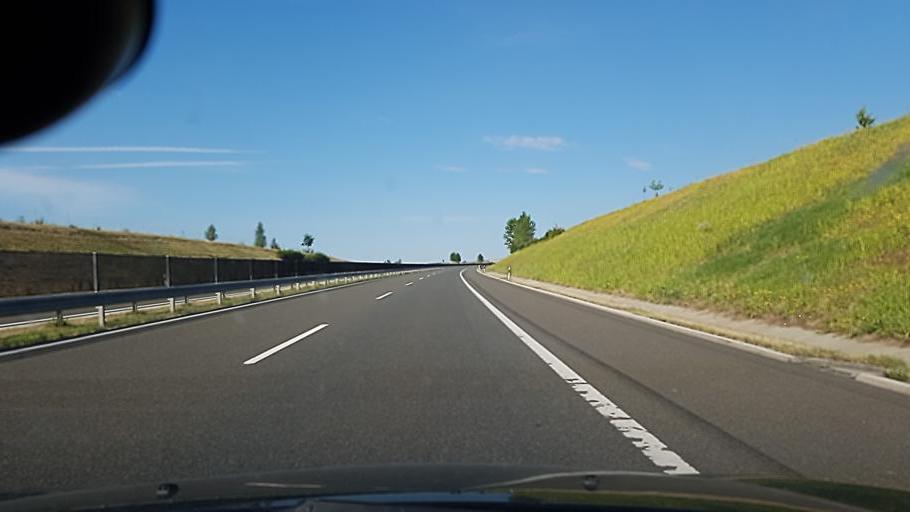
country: HU
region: Tolna
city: Paks
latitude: 46.7001
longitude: 18.8634
